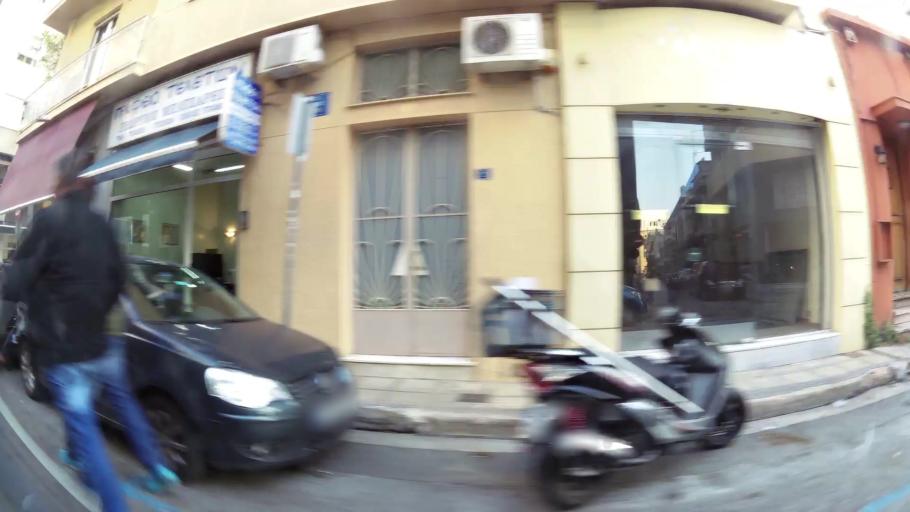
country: GR
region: Attica
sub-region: Nomarchia Athinas
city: Kaisariani
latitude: 37.9842
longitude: 23.7613
